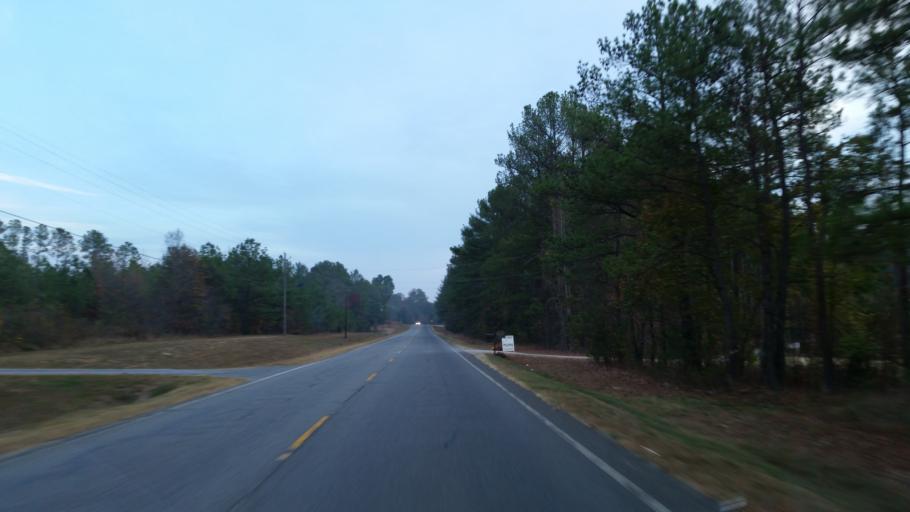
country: US
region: Georgia
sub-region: Murray County
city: Chatsworth
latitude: 34.5981
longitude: -84.7540
